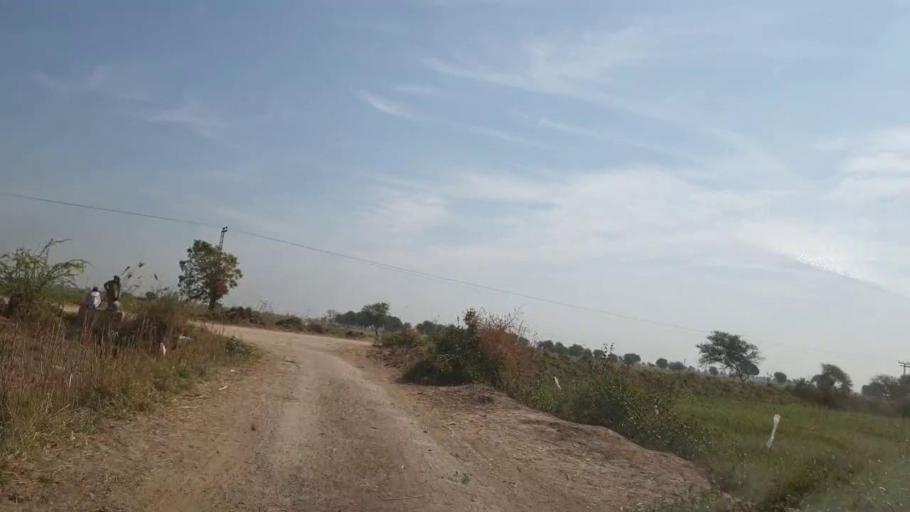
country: PK
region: Sindh
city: Pithoro
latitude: 25.5774
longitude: 69.2013
